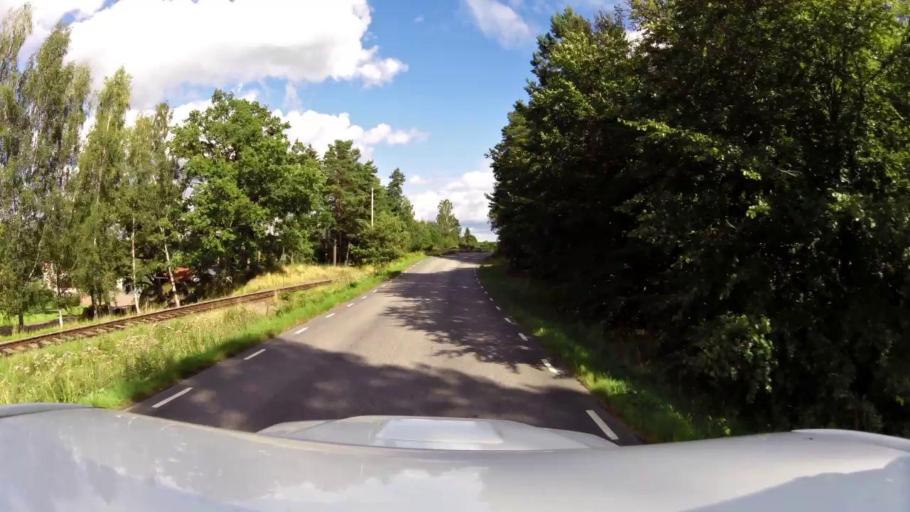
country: SE
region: OEstergoetland
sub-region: Kinda Kommun
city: Rimforsa
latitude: 58.2277
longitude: 15.7164
